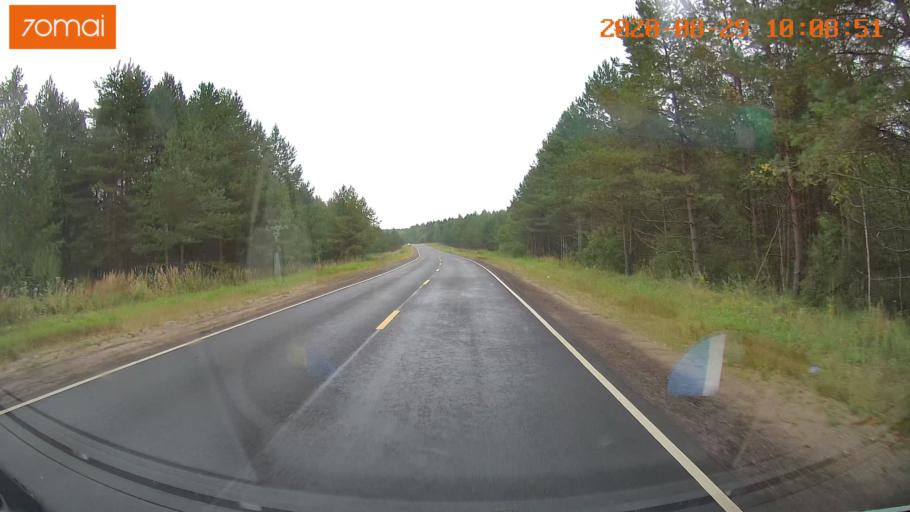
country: RU
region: Ivanovo
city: Kuznechikha
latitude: 57.3744
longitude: 42.6009
